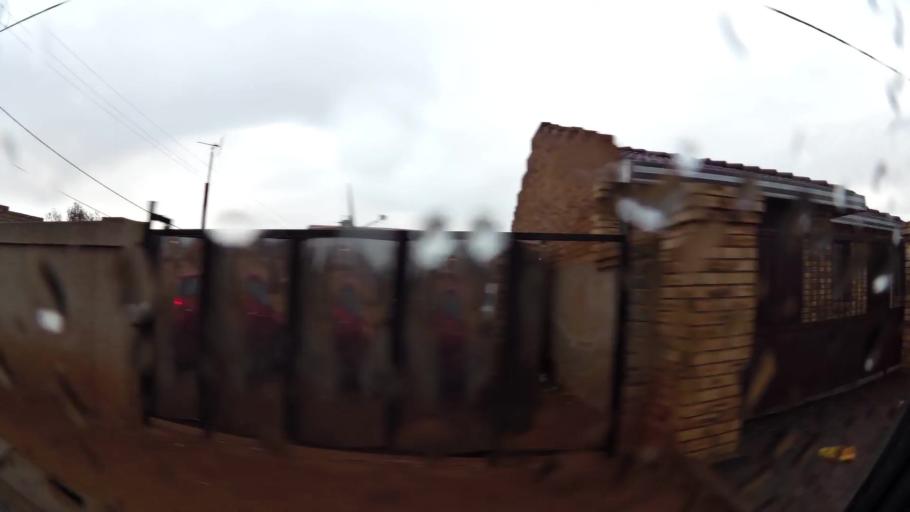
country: ZA
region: Gauteng
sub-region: West Rand District Municipality
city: Randfontein
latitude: -26.1751
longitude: 27.7803
